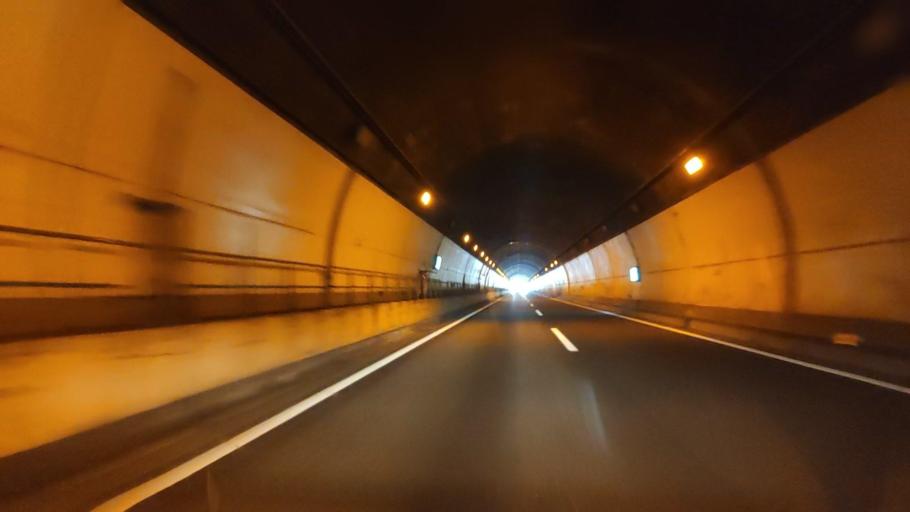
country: JP
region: Akita
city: Hanawa
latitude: 40.0156
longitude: 140.9862
